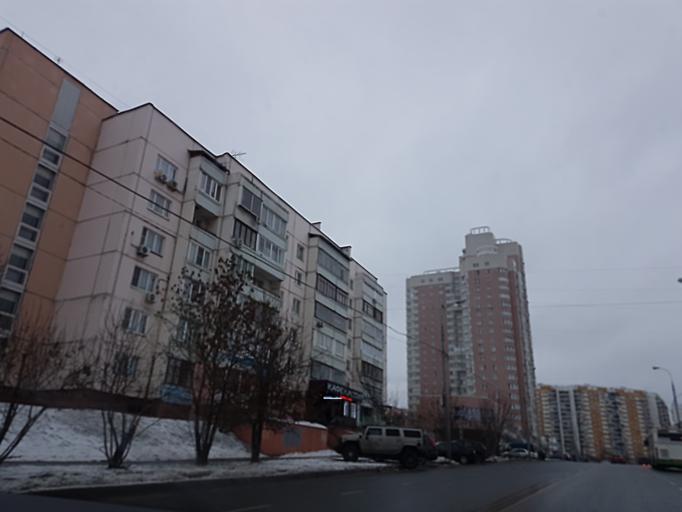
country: RU
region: Moskovskaya
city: Pavshino
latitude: 55.8294
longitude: 37.3540
